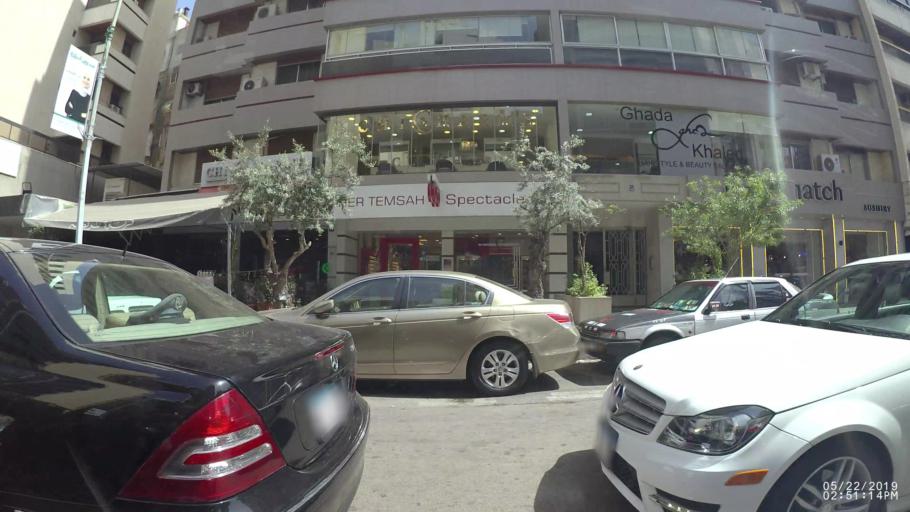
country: LB
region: Beyrouth
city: Ra's Bayrut
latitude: 33.8901
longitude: 35.4803
